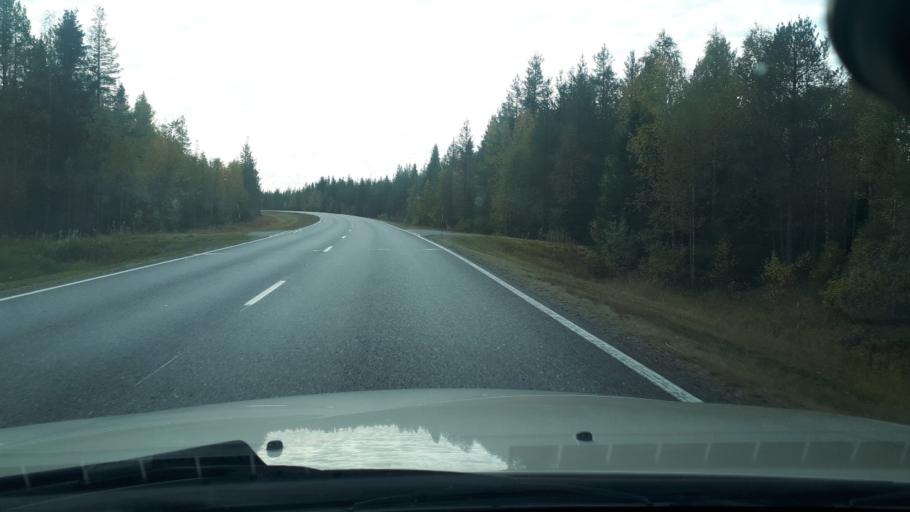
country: FI
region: Lapland
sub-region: Rovaniemi
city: Ranua
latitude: 65.9951
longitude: 26.3395
